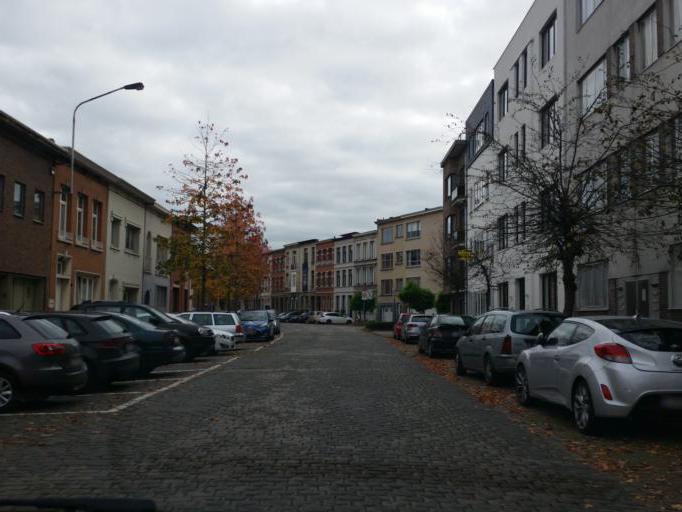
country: BE
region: Flanders
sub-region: Provincie Antwerpen
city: Mortsel
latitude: 51.1813
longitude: 4.4249
